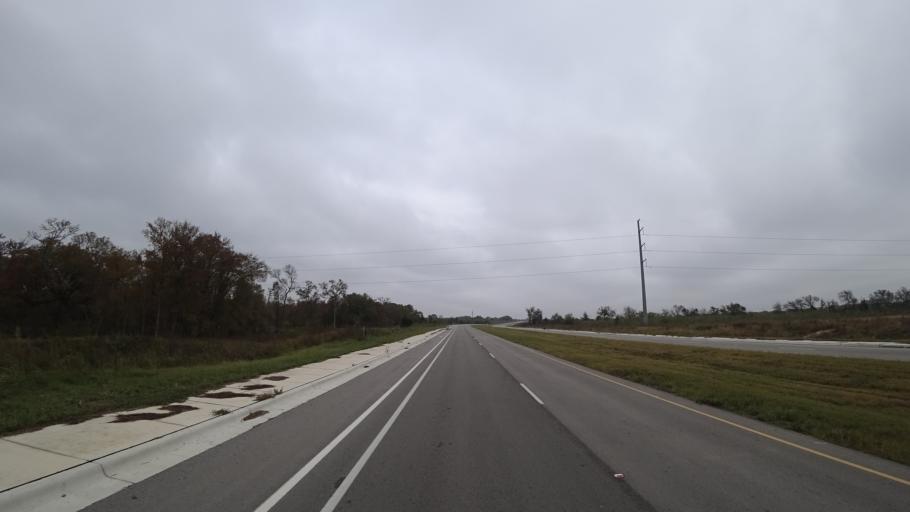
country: US
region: Texas
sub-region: Travis County
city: Pflugerville
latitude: 30.4077
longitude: -97.6120
